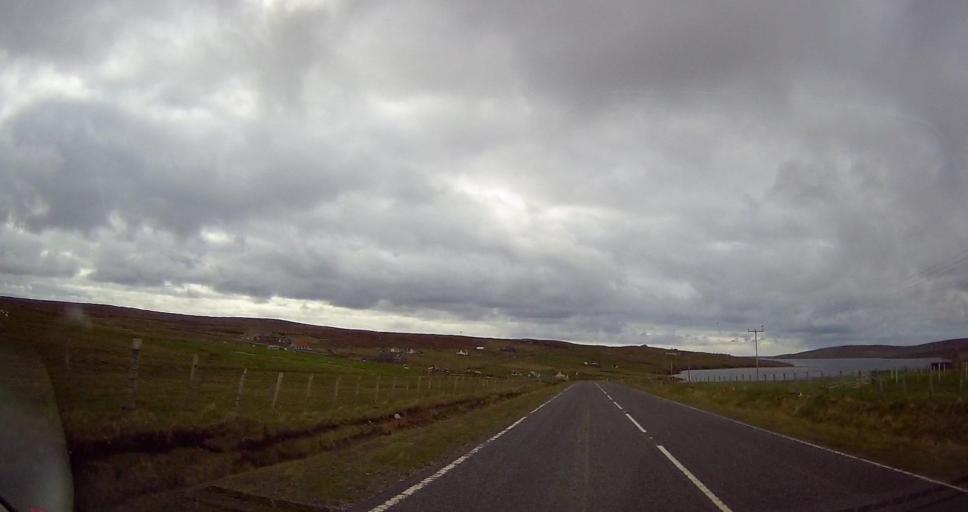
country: GB
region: Scotland
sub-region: Shetland Islands
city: Shetland
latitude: 60.6638
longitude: -1.0545
